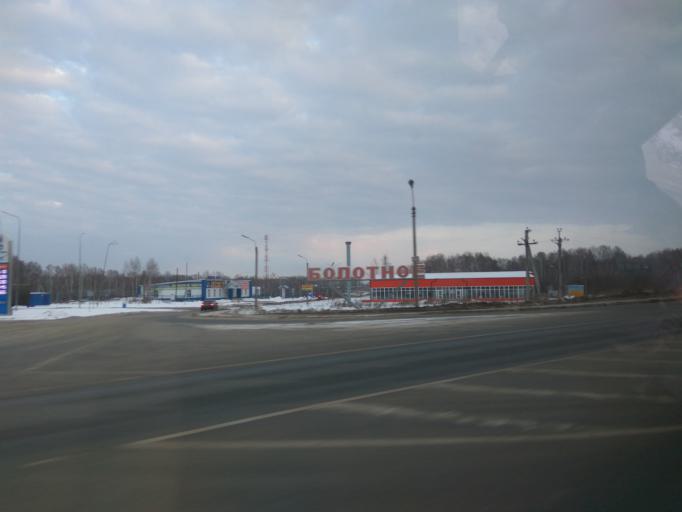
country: RU
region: Novosibirsk
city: Bolotnoye
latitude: 55.6458
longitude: 84.3583
